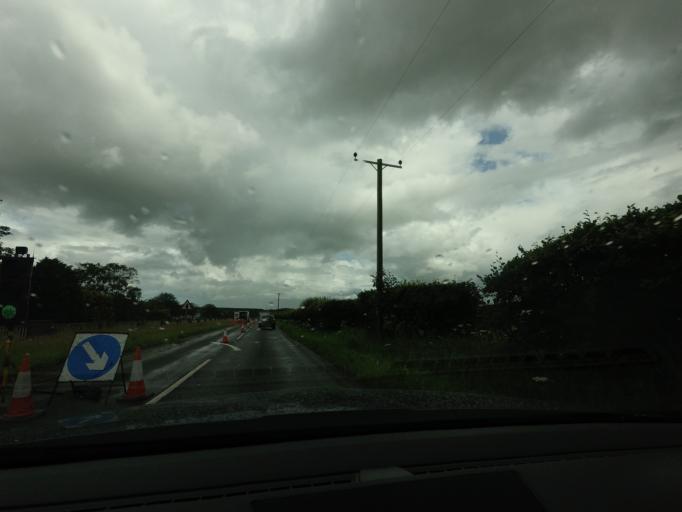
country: GB
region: Scotland
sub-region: Aberdeenshire
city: Turriff
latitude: 57.5502
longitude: -2.4420
